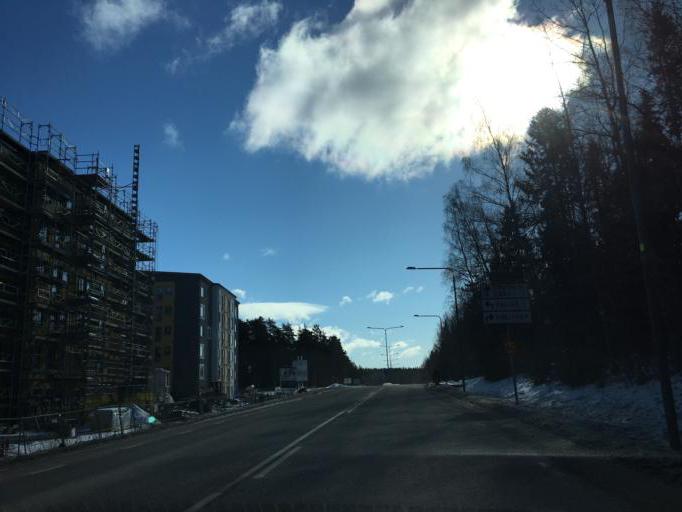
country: SE
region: Vaestmanland
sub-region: Vasteras
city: Vasteras
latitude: 59.6220
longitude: 16.4969
